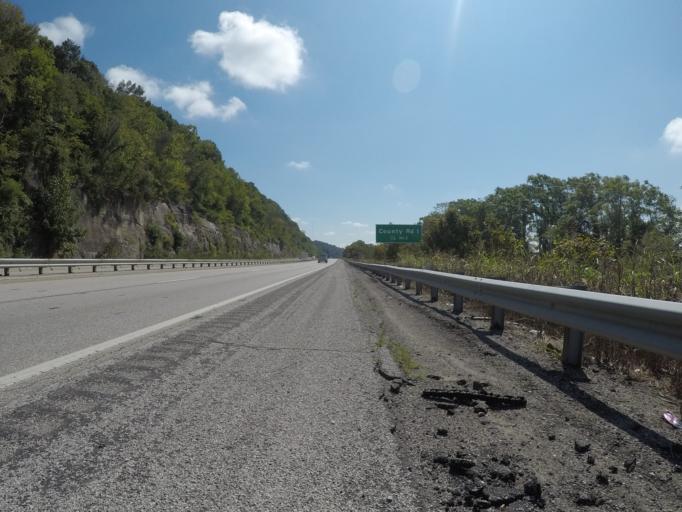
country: US
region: Kentucky
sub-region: Boyd County
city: Ashland
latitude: 38.4760
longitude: -82.6146
